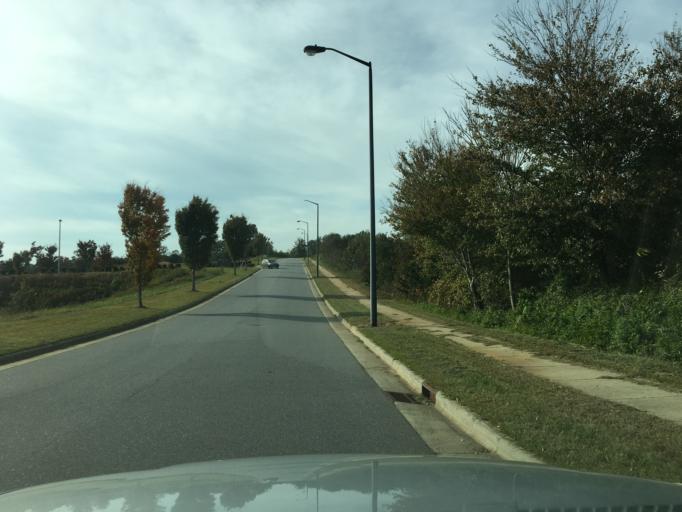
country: US
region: North Carolina
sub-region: Catawba County
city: Saint Stephens
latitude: 35.7264
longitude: -81.2840
